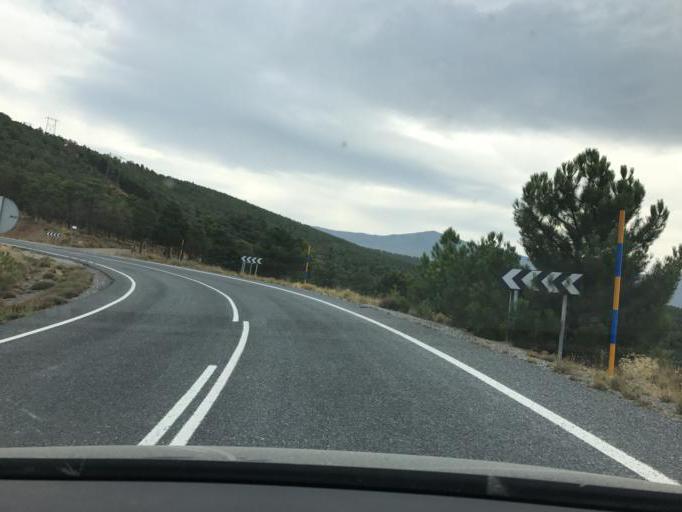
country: ES
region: Andalusia
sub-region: Provincia de Granada
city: Aldeire
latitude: 37.1454
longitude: -3.0504
